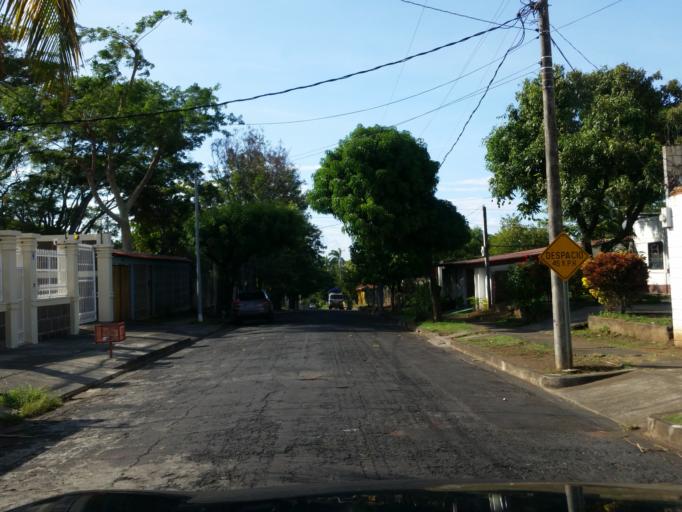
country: NI
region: Managua
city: Managua
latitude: 12.1184
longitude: -86.2640
